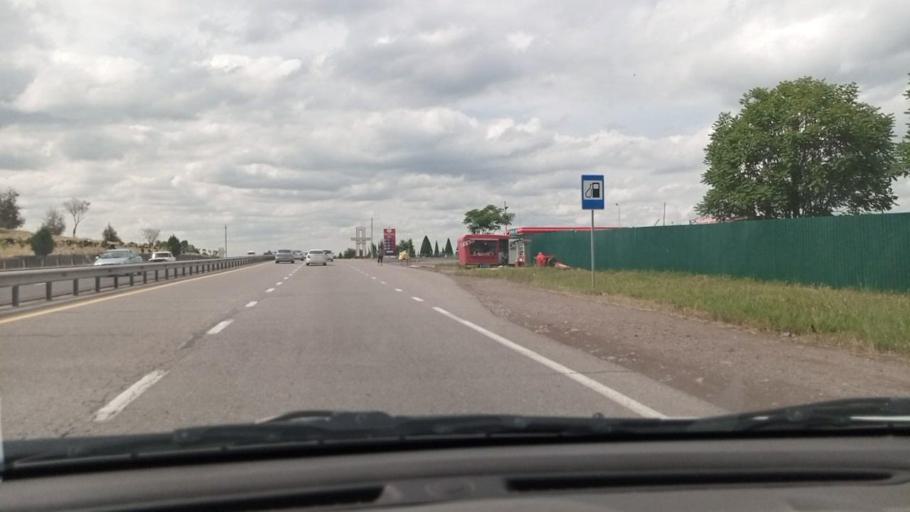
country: UZ
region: Toshkent
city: Tuytepa
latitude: 41.1211
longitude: 69.4415
